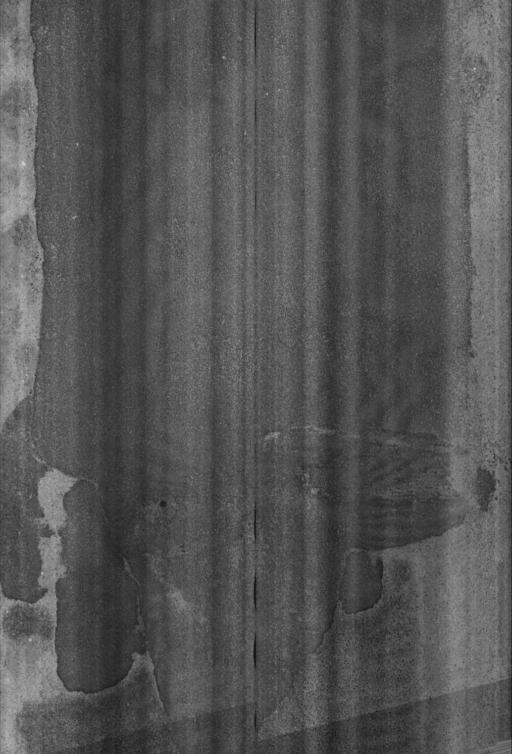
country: US
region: Maryland
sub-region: Montgomery County
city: Chevy Chase
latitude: 38.9670
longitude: -77.0522
